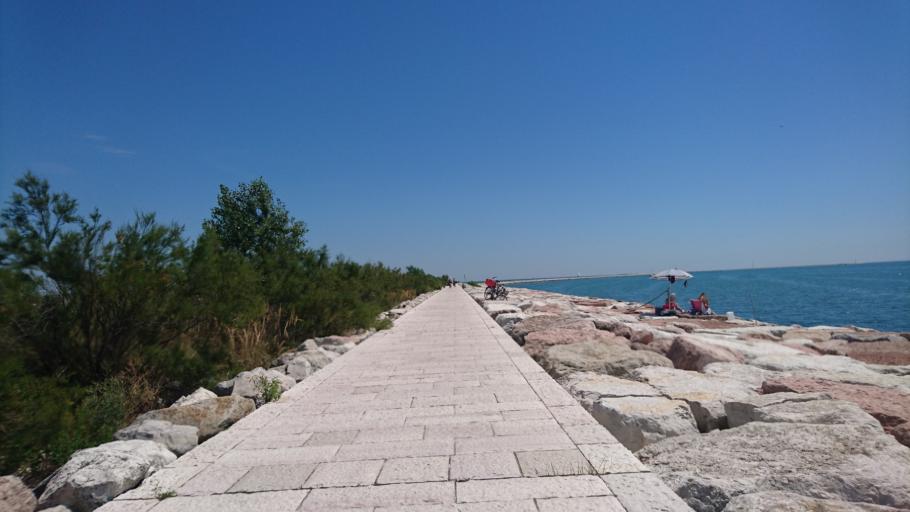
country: IT
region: Veneto
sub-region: Provincia di Venezia
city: Lido
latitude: 45.4280
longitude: 12.4078
